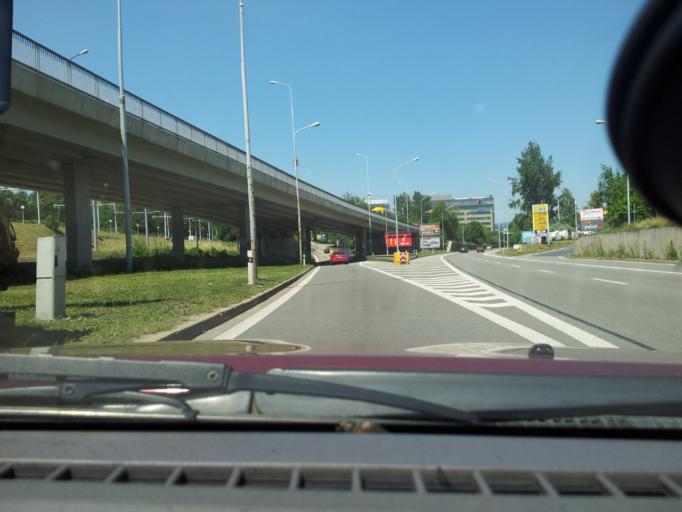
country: CZ
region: South Moravian
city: Moravany
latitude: 49.1673
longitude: 16.5989
